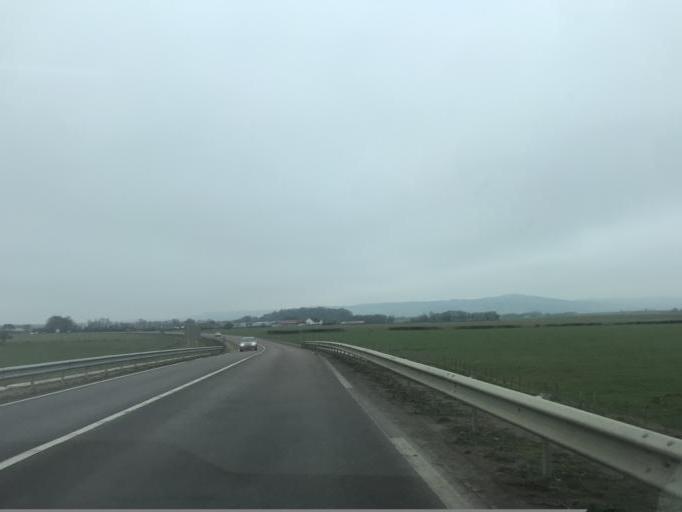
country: FR
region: Bourgogne
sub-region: Departement de l'Yonne
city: Avallon
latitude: 47.5029
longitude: 3.9073
